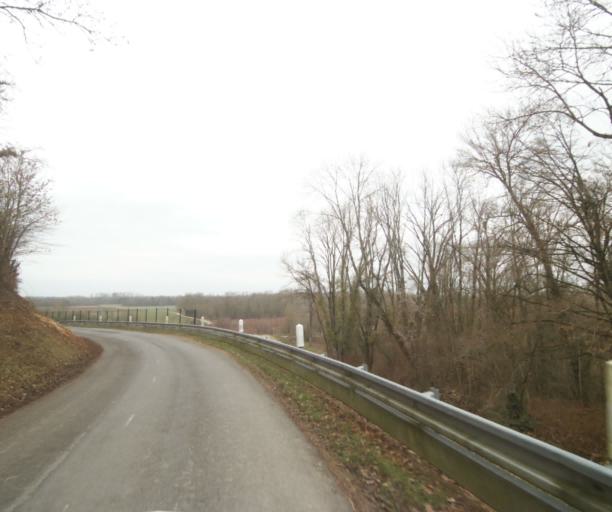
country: FR
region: Champagne-Ardenne
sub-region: Departement de la Haute-Marne
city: Villiers-en-Lieu
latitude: 48.6356
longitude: 4.8373
